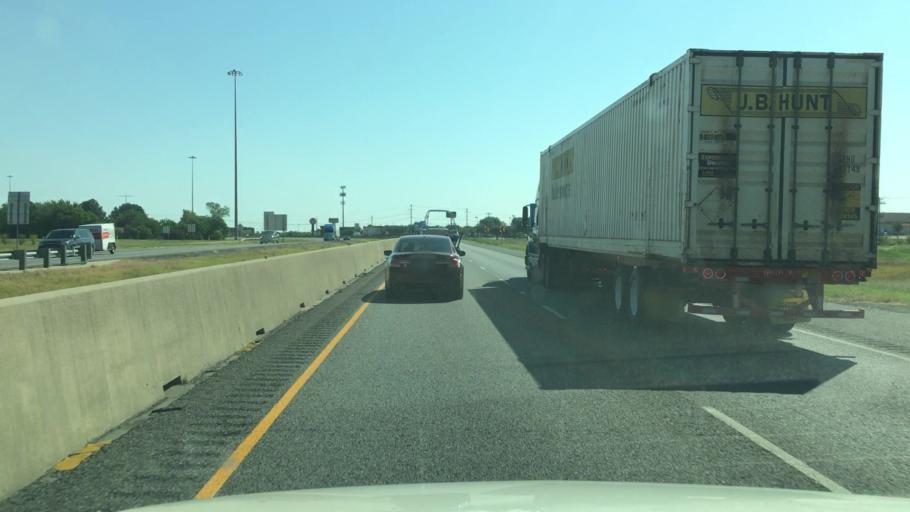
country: US
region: Texas
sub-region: Hunt County
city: Greenville
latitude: 33.0965
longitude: -96.1094
